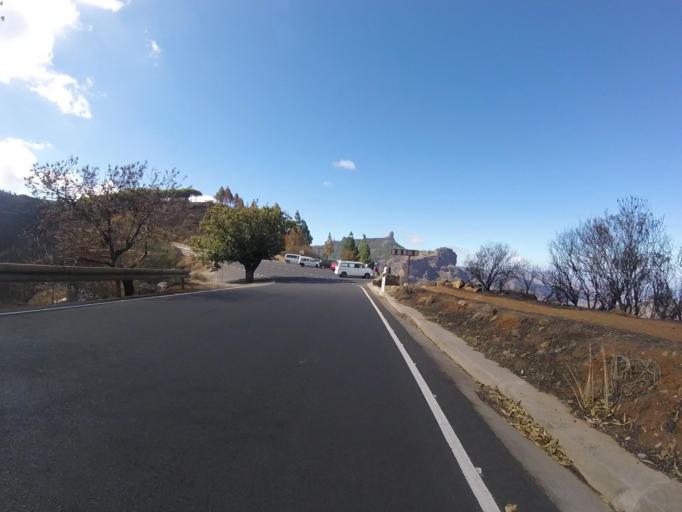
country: ES
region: Canary Islands
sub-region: Provincia de Las Palmas
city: Tejeda
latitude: 27.9892
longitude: -15.5930
